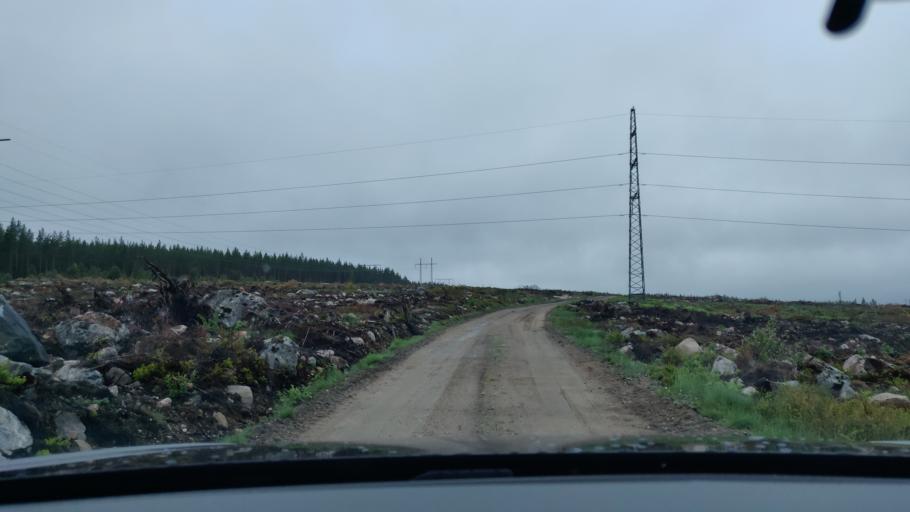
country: SE
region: Dalarna
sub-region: Avesta Kommun
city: Horndal
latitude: 60.3115
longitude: 16.4007
